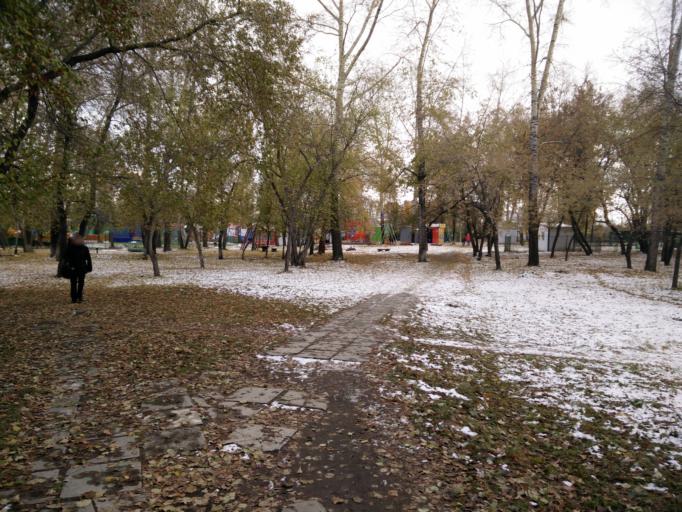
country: RU
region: Novosibirsk
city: Berdsk
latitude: 54.7588
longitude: 83.1019
